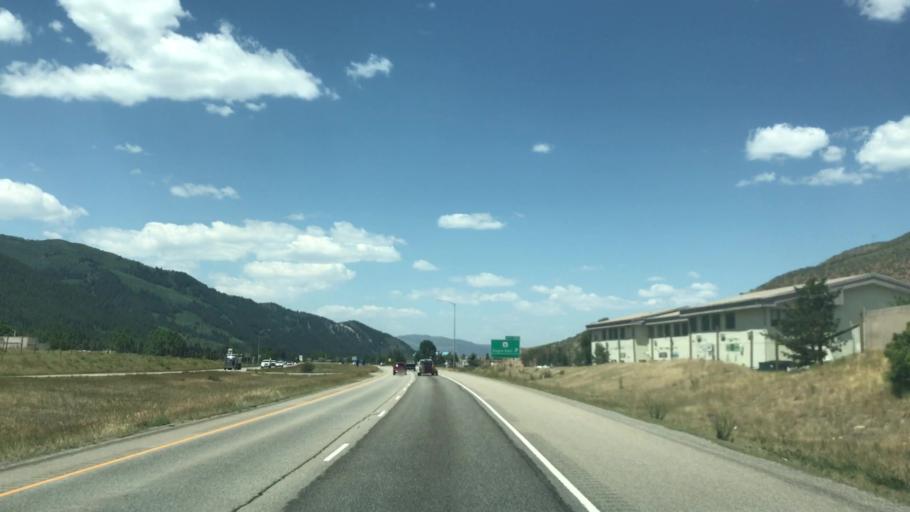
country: US
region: Colorado
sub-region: Eagle County
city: Avon
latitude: 39.6206
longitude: -106.4723
